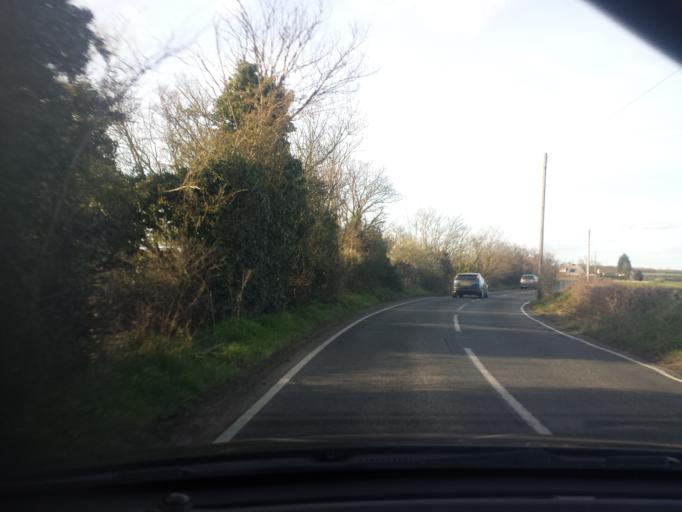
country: GB
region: England
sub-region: Essex
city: Little Clacton
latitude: 51.8088
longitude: 1.1260
